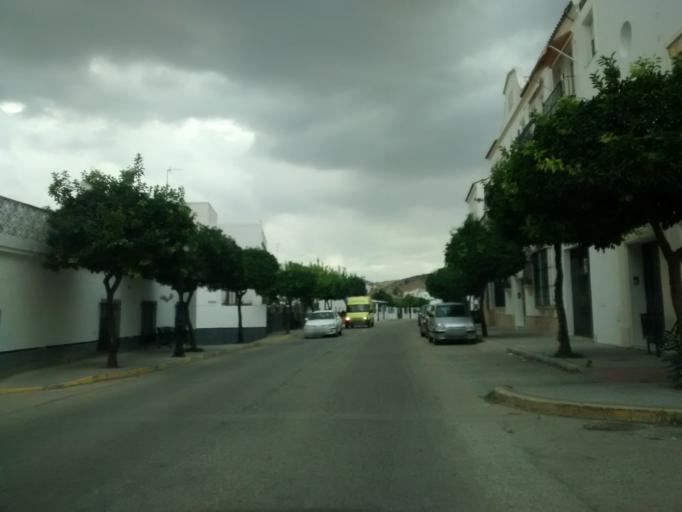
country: ES
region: Andalusia
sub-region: Provincia de Cadiz
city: Bornos
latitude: 36.8197
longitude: -5.7451
